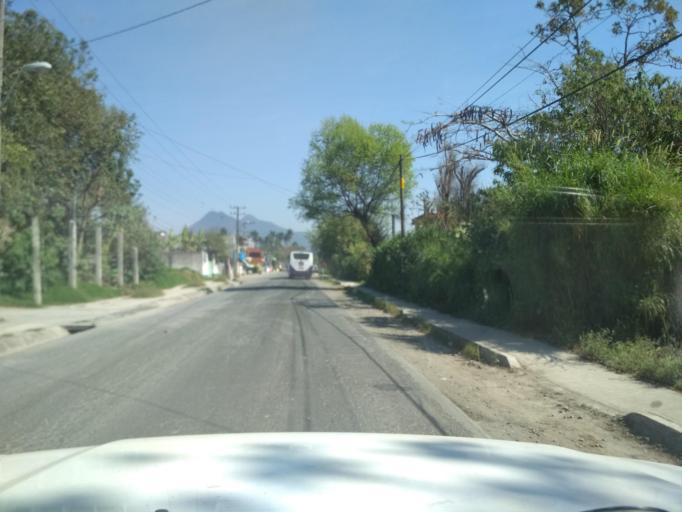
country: MX
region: Veracruz
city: Jalapilla
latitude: 18.8179
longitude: -97.0900
